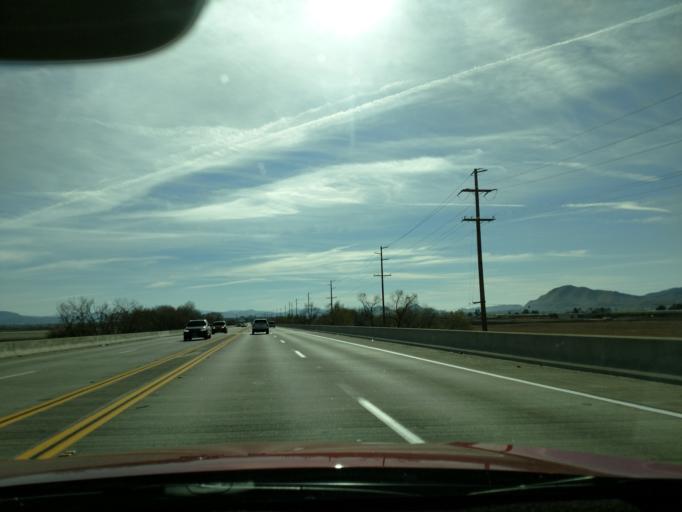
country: US
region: California
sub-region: Riverside County
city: San Jacinto
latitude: 33.8336
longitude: -117.0036
